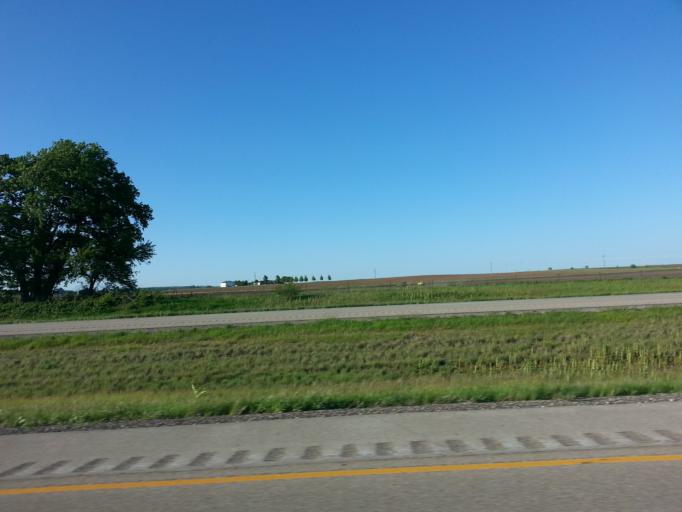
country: US
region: Illinois
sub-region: McLean County
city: Le Roy
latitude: 40.3623
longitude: -88.8158
